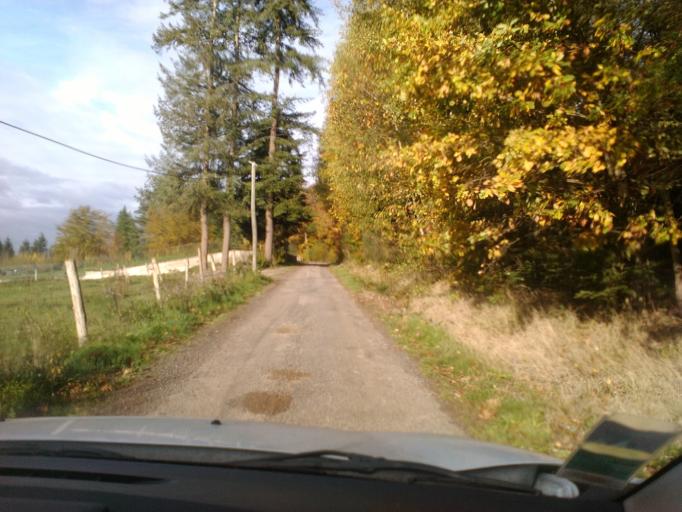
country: FR
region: Lorraine
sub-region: Departement des Vosges
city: Moyenmoutier
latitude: 48.4195
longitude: 6.8754
